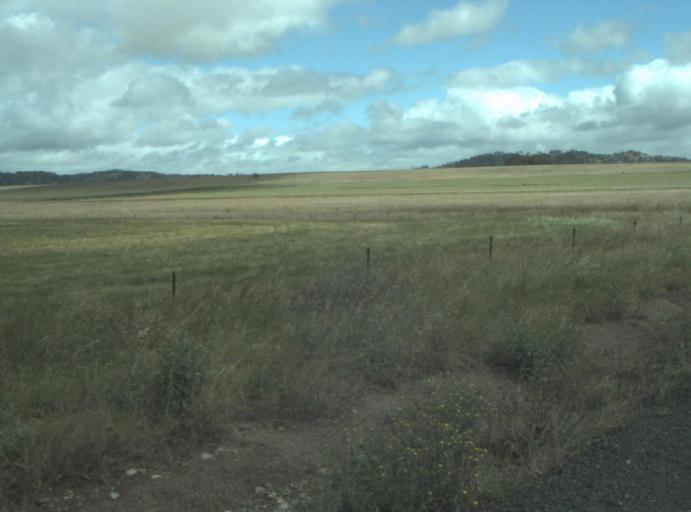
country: AU
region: Victoria
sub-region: Greater Geelong
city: Lara
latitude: -37.9025
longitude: 144.3172
